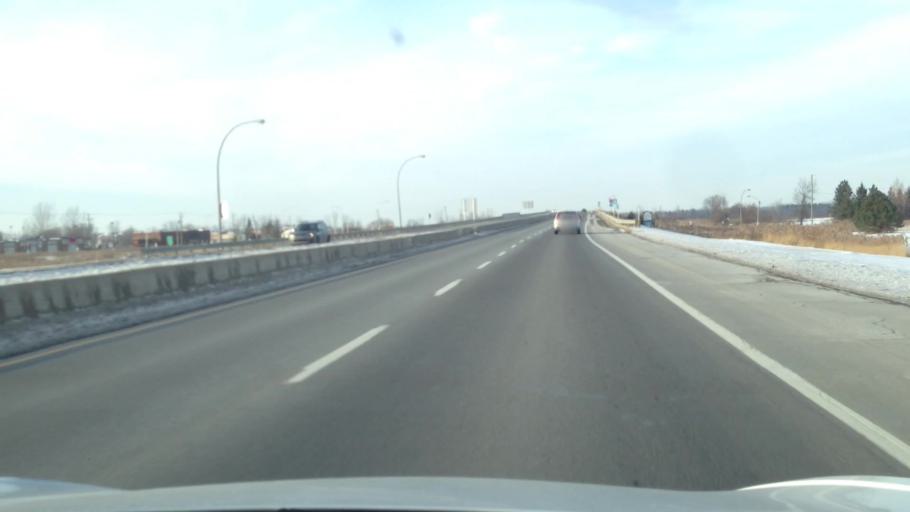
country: CA
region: Quebec
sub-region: Monteregie
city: Rigaud
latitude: 45.4780
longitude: -74.2829
